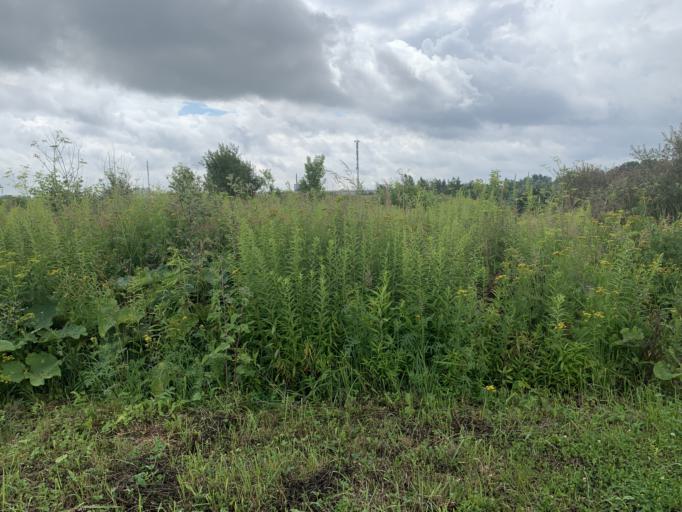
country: RU
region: Moskovskaya
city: Mamontovka
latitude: 55.9701
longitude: 37.8384
